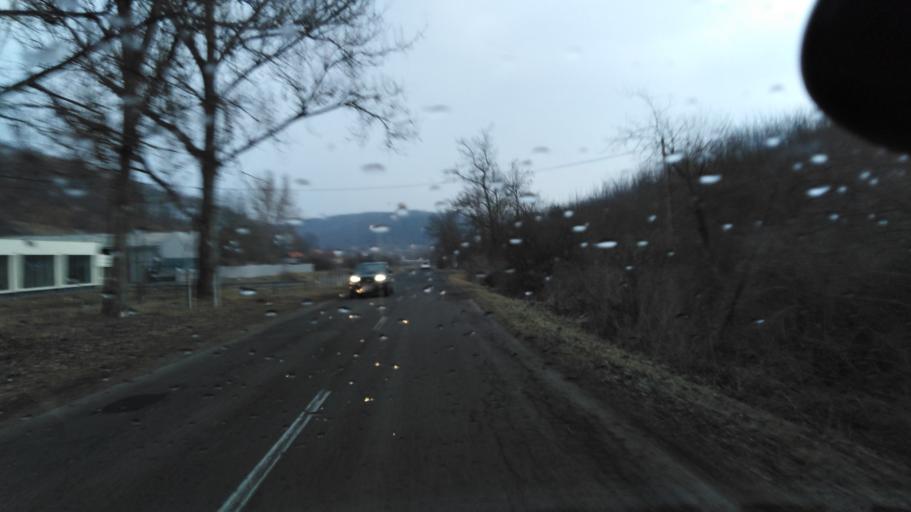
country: HU
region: Nograd
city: Salgotarjan
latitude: 48.0513
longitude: 19.7764
